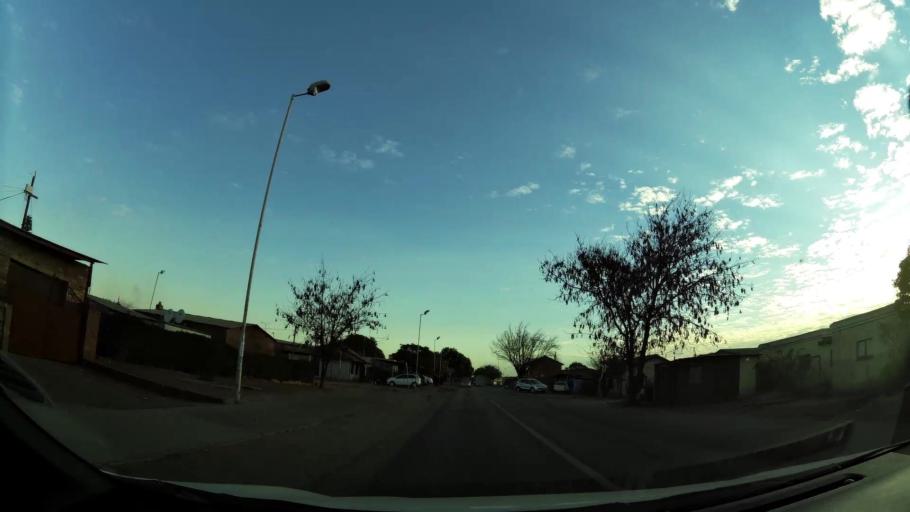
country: ZA
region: Gauteng
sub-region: City of Tshwane Metropolitan Municipality
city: Pretoria
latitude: -25.7138
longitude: 28.3554
